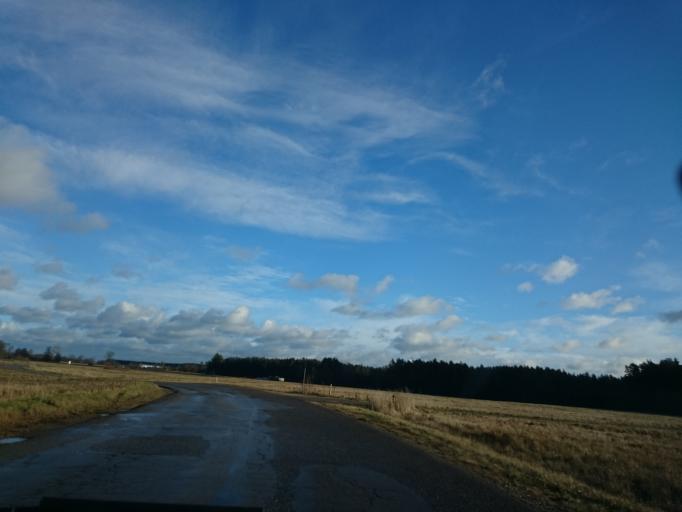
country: LV
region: Garkalne
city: Garkalne
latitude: 57.0636
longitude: 24.3808
